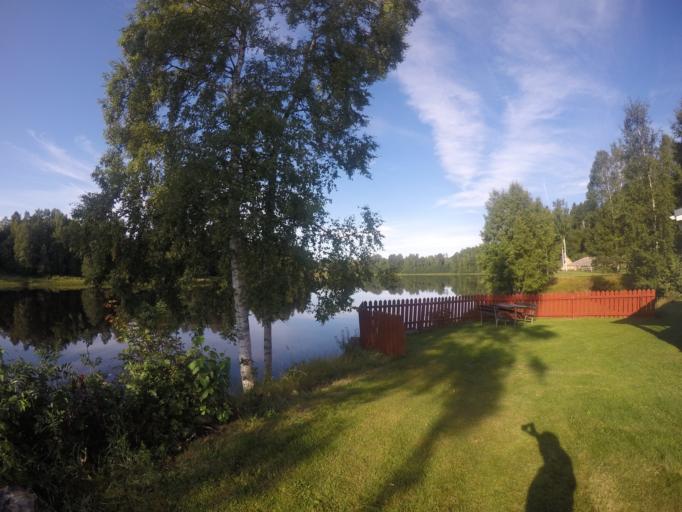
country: SE
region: Dalarna
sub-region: Gagnefs Kommun
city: Gagnef
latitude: 60.5337
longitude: 15.0615
